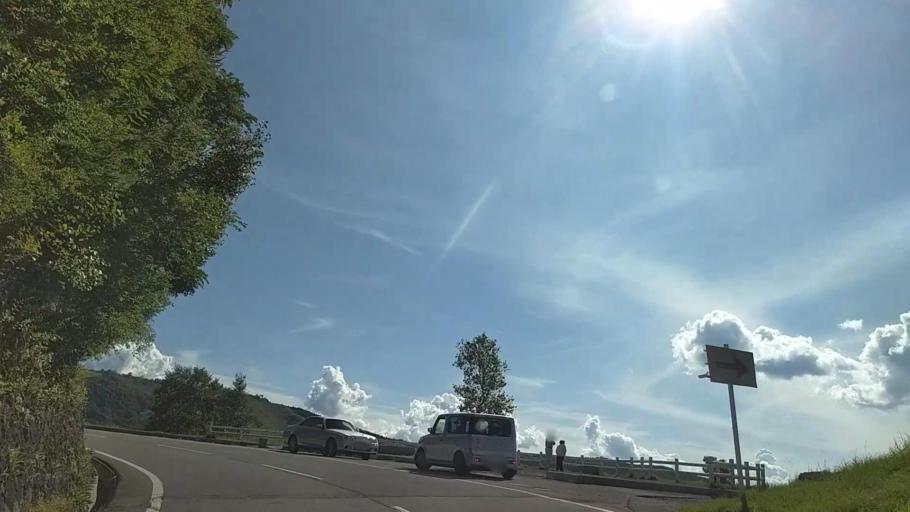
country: JP
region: Nagano
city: Chino
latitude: 36.1053
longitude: 138.2714
